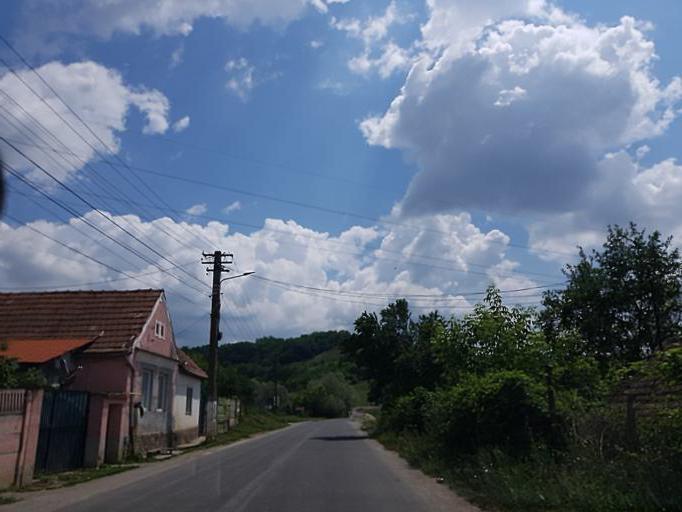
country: RO
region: Sibiu
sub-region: Comuna Seica Mica
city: Seica Mica
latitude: 46.0522
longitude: 24.1428
